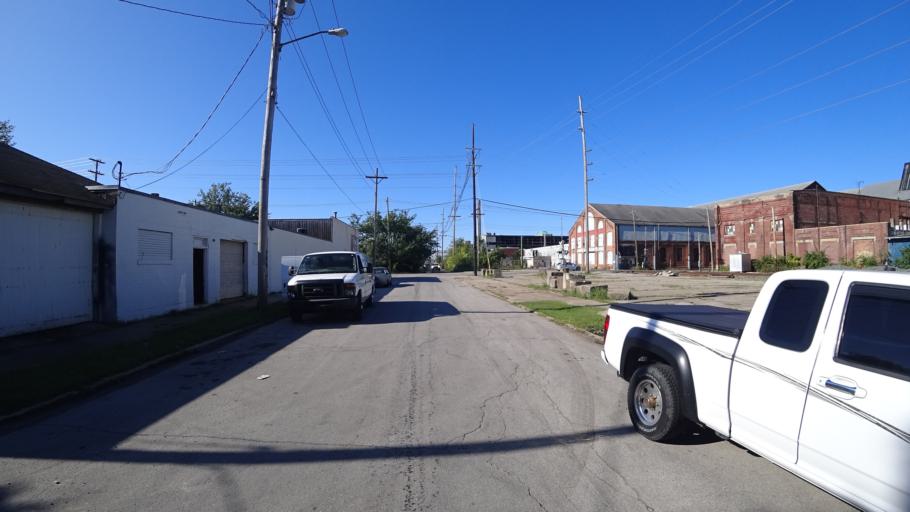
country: US
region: Ohio
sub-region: Butler County
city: Hamilton
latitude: 39.4036
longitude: -84.5547
